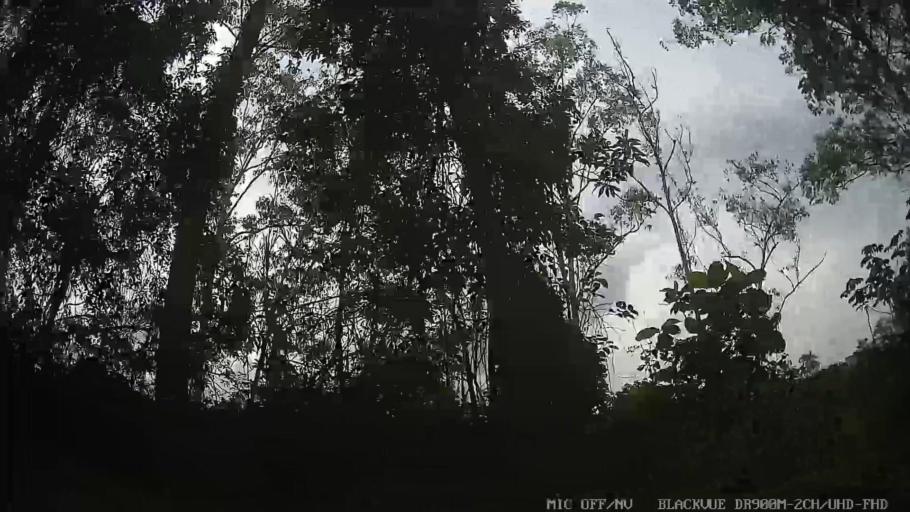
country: BR
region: Sao Paulo
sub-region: Aruja
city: Aruja
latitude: -23.4013
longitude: -46.2362
